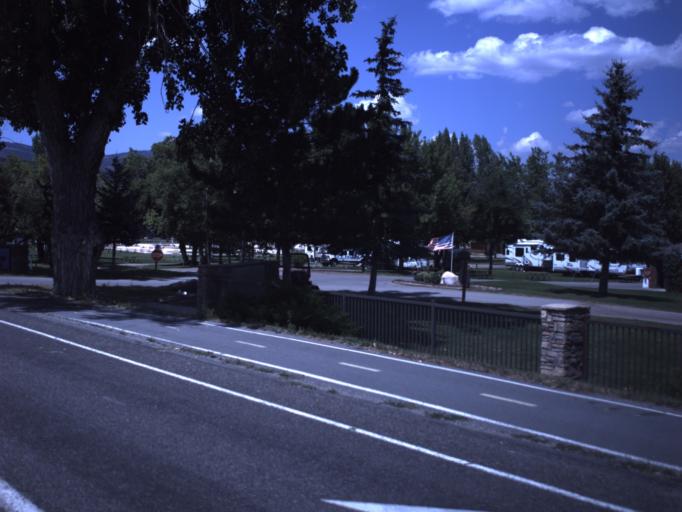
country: US
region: Utah
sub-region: Rich County
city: Randolph
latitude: 41.9077
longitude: -111.3844
